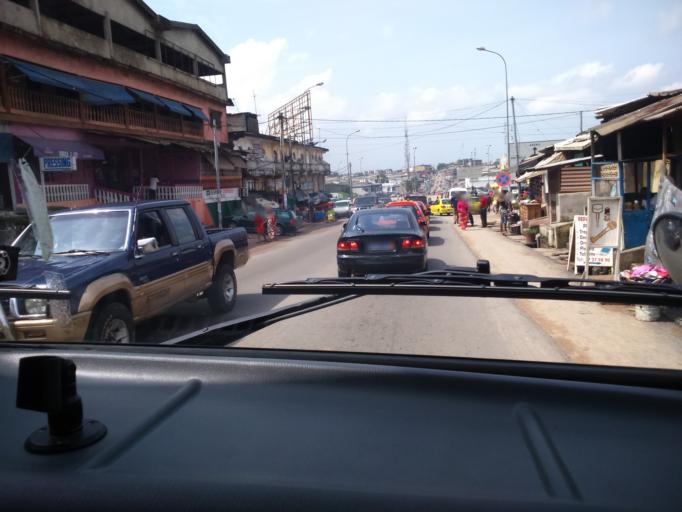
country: CI
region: Lagunes
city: Abidjan
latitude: 5.3548
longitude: -3.9775
